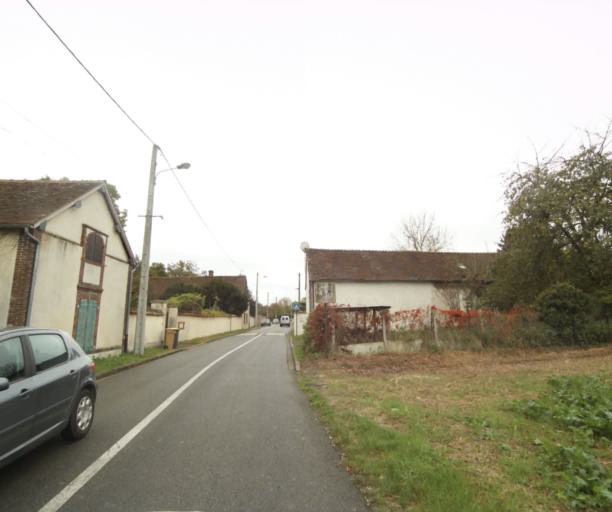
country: FR
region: Centre
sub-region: Departement d'Eure-et-Loir
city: Dreux
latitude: 48.7604
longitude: 1.3550
